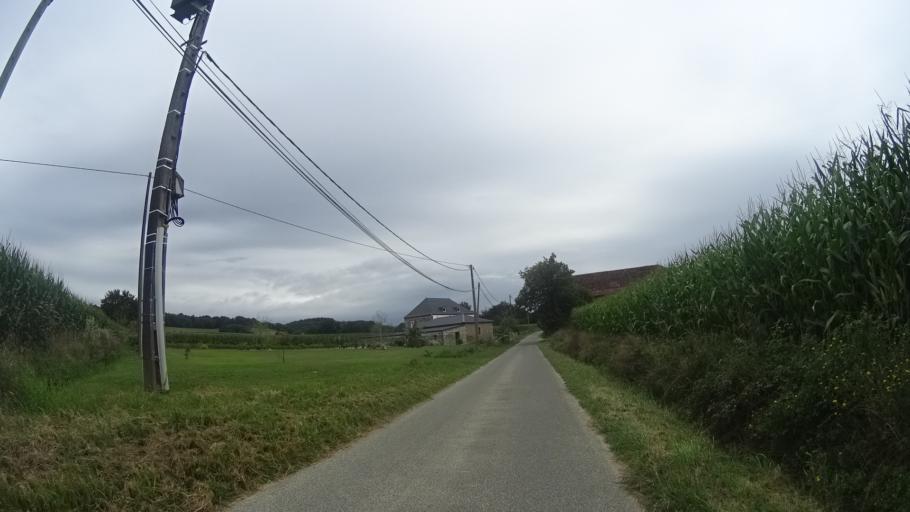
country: FR
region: Aquitaine
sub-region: Departement des Pyrenees-Atlantiques
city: Orthez
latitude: 43.4864
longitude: -0.7174
